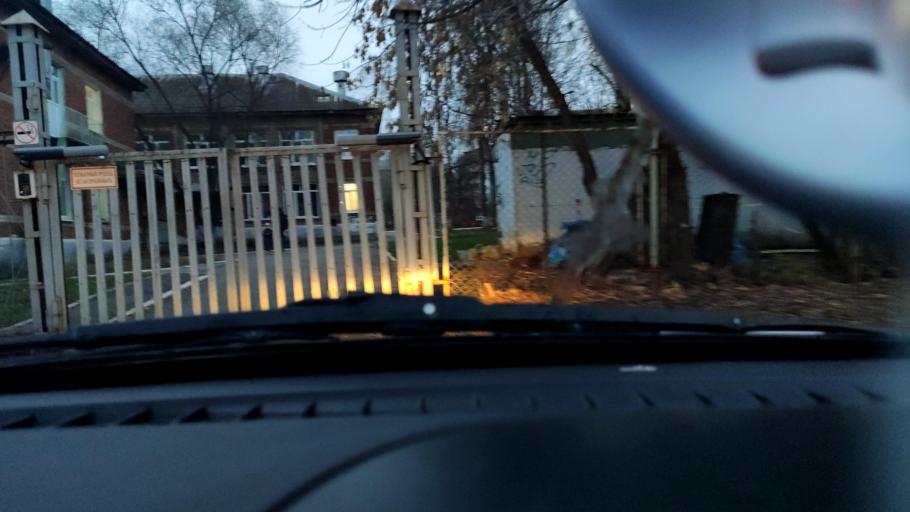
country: RU
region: Perm
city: Perm
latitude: 57.9812
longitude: 56.1841
